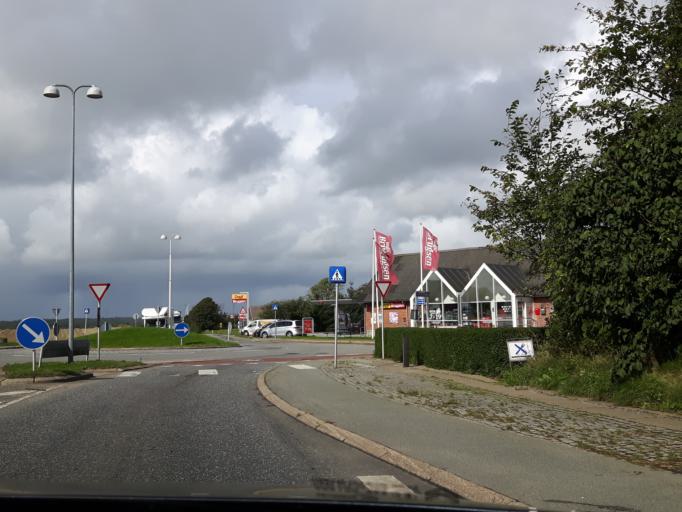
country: DK
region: North Denmark
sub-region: Morso Kommune
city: Nykobing Mors
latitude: 57.0353
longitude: 8.9708
